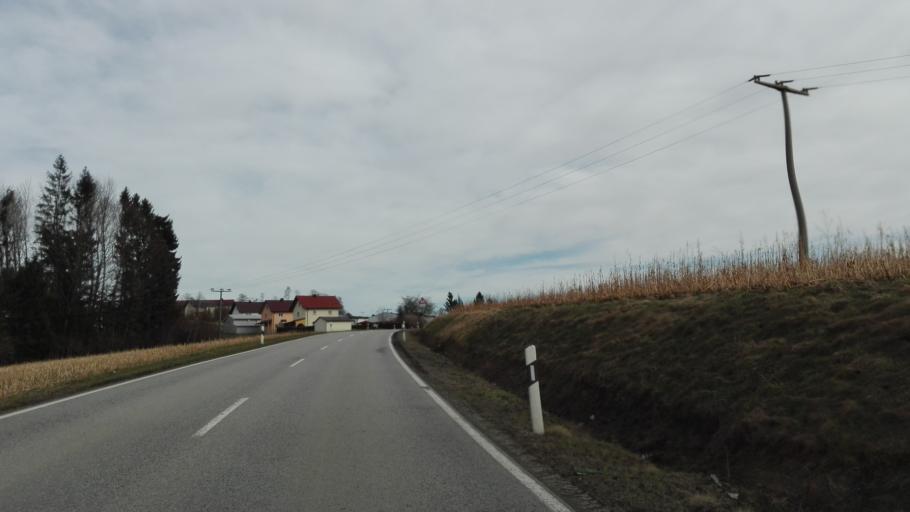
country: DE
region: Bavaria
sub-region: Lower Bavaria
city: Hauzenberg
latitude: 48.6391
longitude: 13.6374
